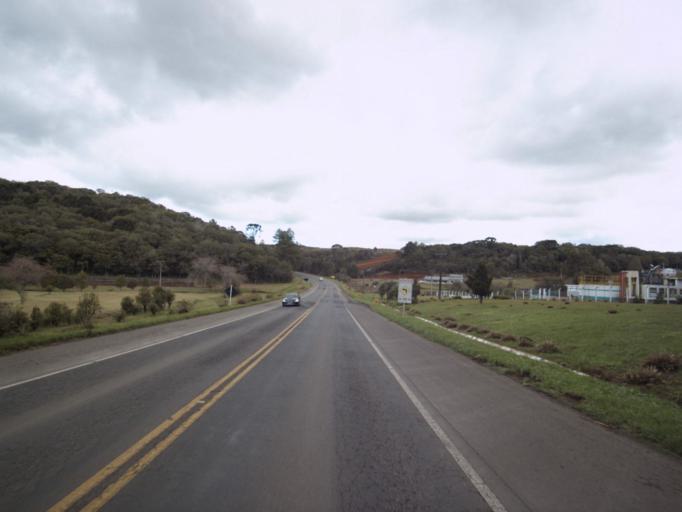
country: BR
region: Santa Catarina
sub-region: Joacaba
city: Joacaba
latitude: -27.0787
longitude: -51.6634
